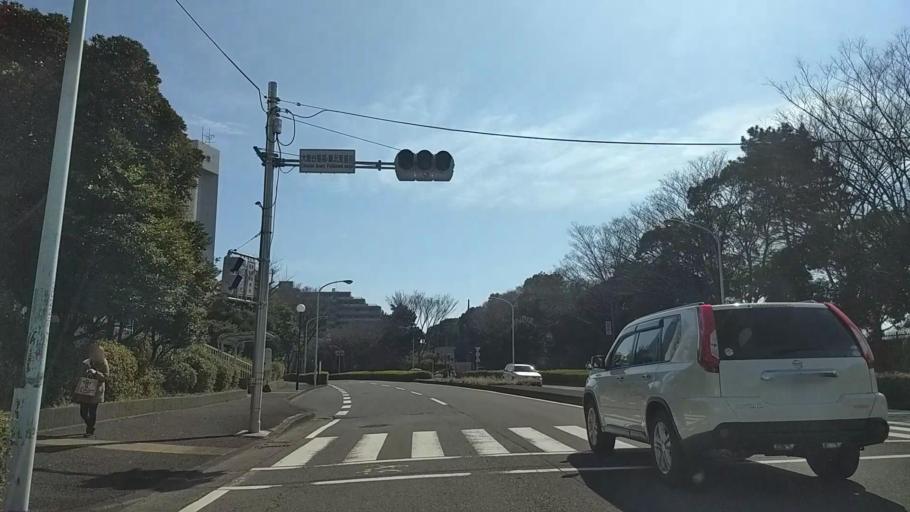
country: JP
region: Kanagawa
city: Fujisawa
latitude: 35.3562
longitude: 139.4427
